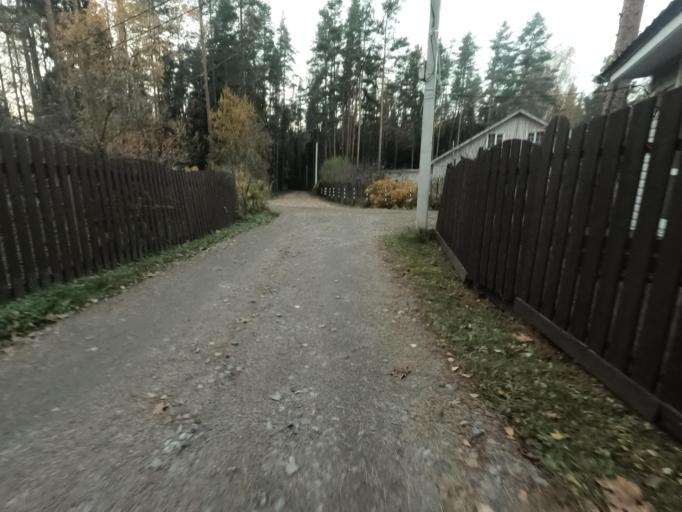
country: RU
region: St.-Petersburg
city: Komarovo
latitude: 60.2007
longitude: 29.8232
